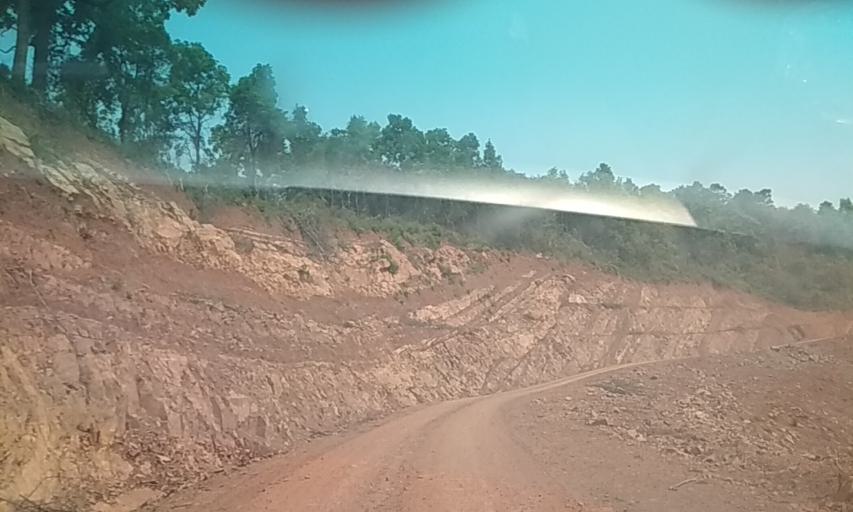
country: VN
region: Huyen Dien Bien
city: Dien Bien Phu
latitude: 21.4735
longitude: 102.7732
